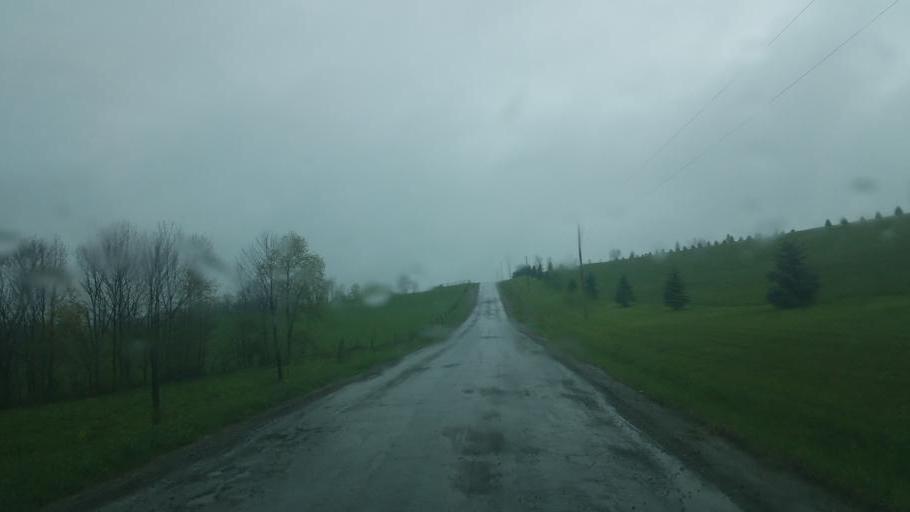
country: US
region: New York
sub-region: Steuben County
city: Canisteo
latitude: 42.1081
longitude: -77.5215
